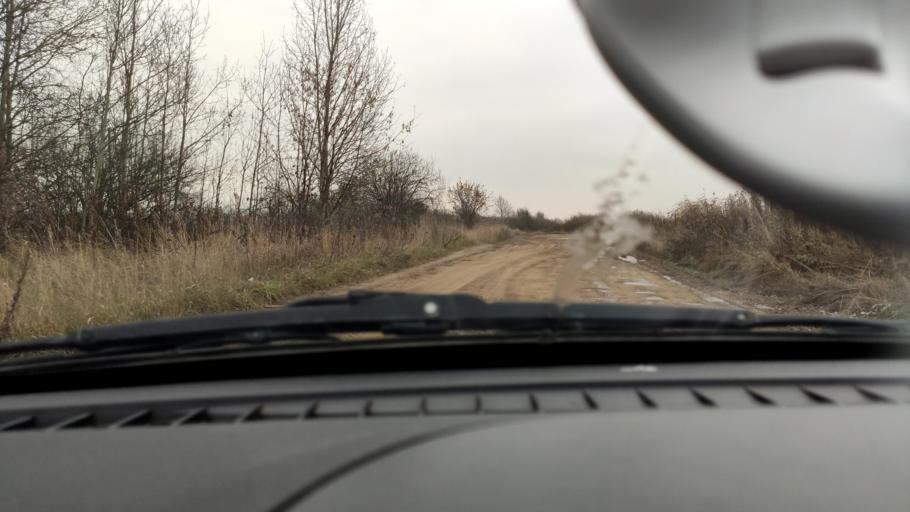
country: RU
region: Perm
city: Kondratovo
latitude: 57.9877
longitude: 56.0795
